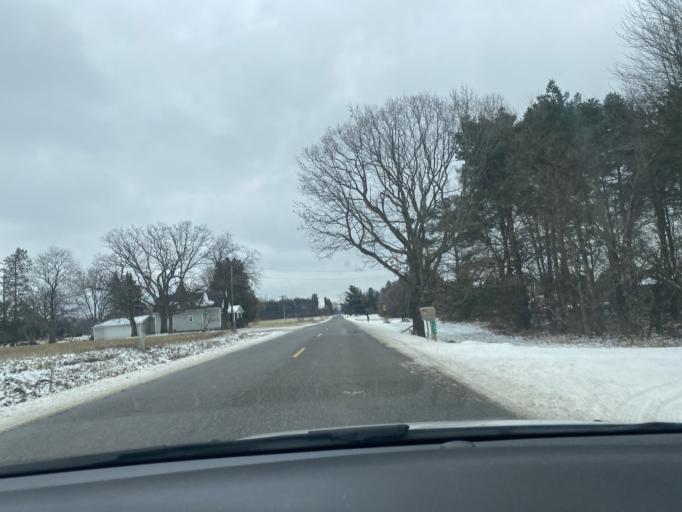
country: US
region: Michigan
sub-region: Lapeer County
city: Barnes Lake-Millers Lake
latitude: 43.2058
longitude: -83.2746
